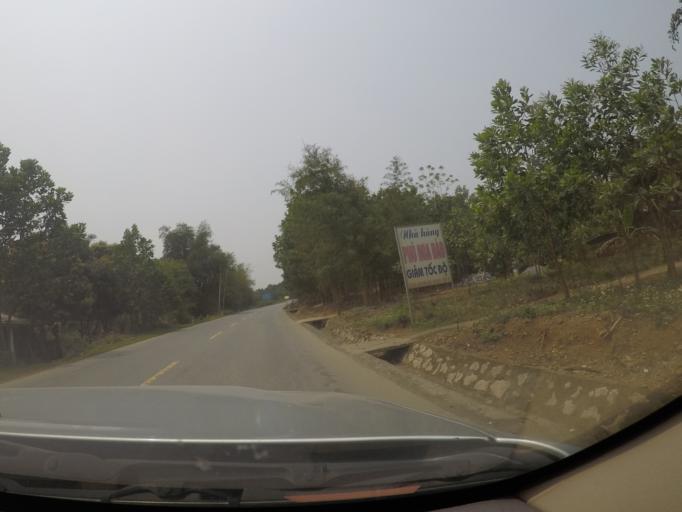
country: VN
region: Thanh Hoa
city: Thi Tran Cam Thuy
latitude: 20.1442
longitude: 105.4332
